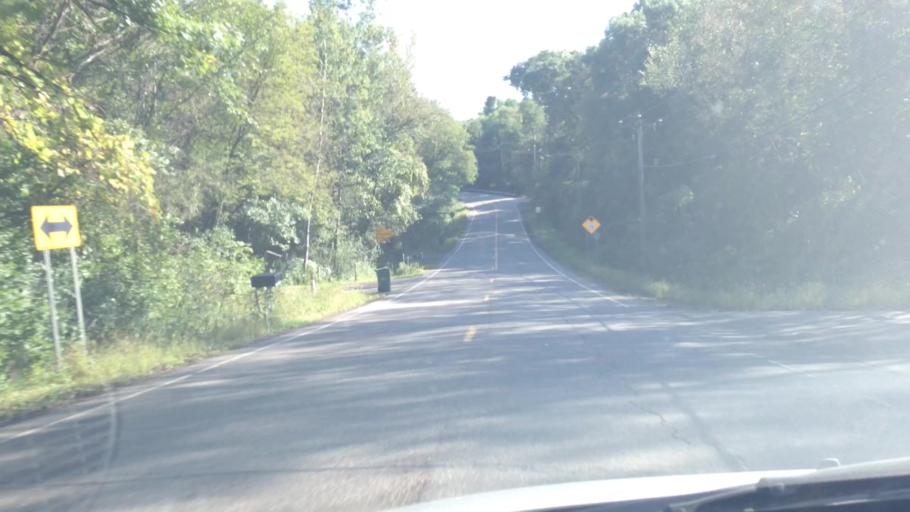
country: US
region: Minnesota
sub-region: Washington County
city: Stillwater
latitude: 45.0845
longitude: -92.8130
